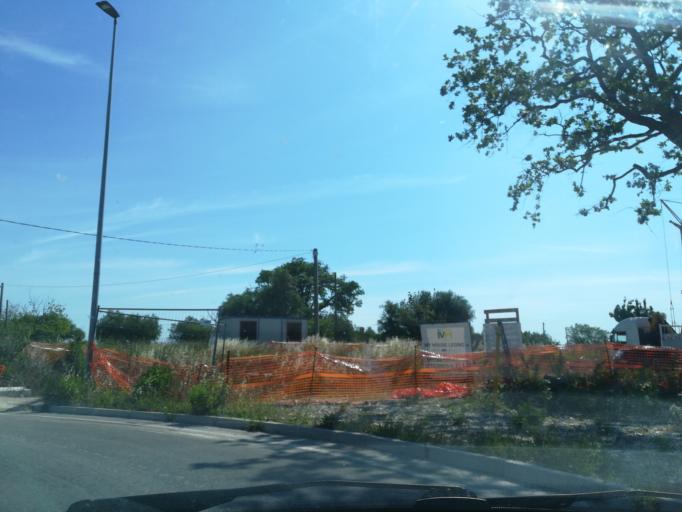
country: IT
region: The Marches
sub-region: Provincia di Macerata
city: Piediripa
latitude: 43.2883
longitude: 13.4778
